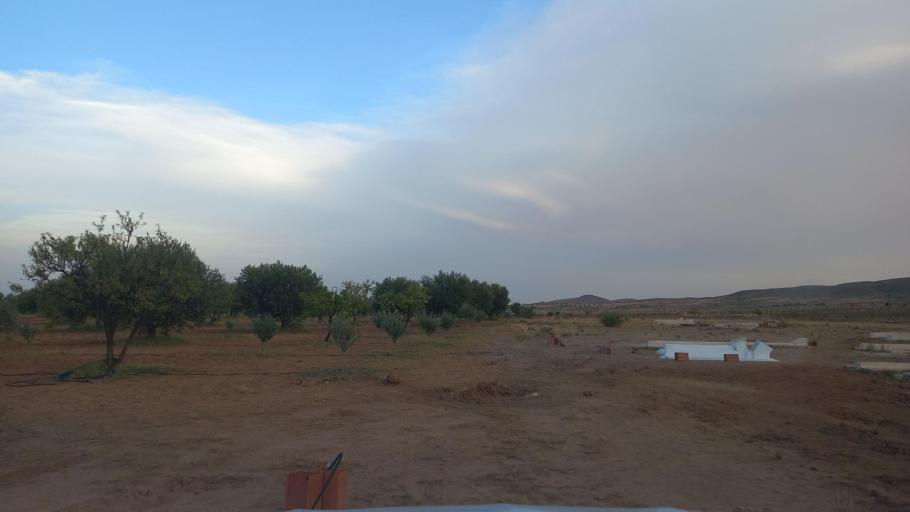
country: TN
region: Al Qasrayn
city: Kasserine
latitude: 35.1886
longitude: 9.0478
